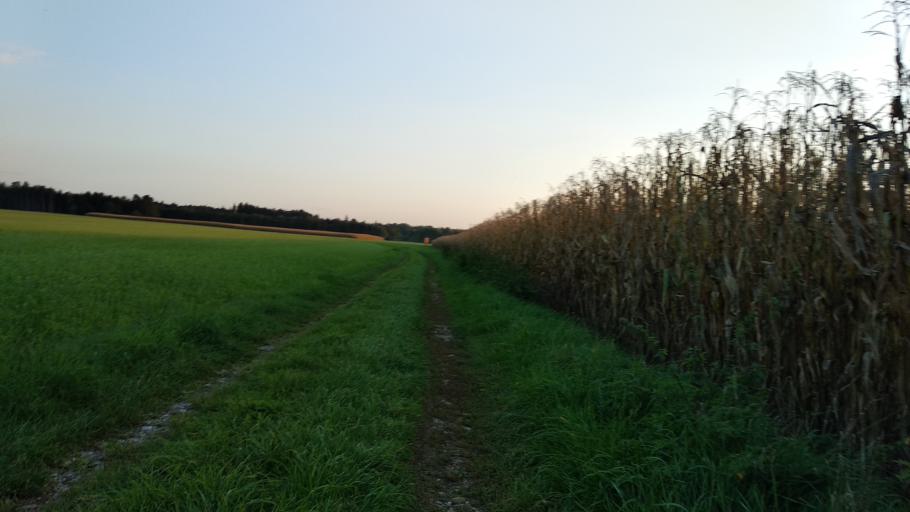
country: DE
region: Bavaria
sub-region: Upper Bavaria
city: Grasbrunn
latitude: 48.0552
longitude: 11.7718
